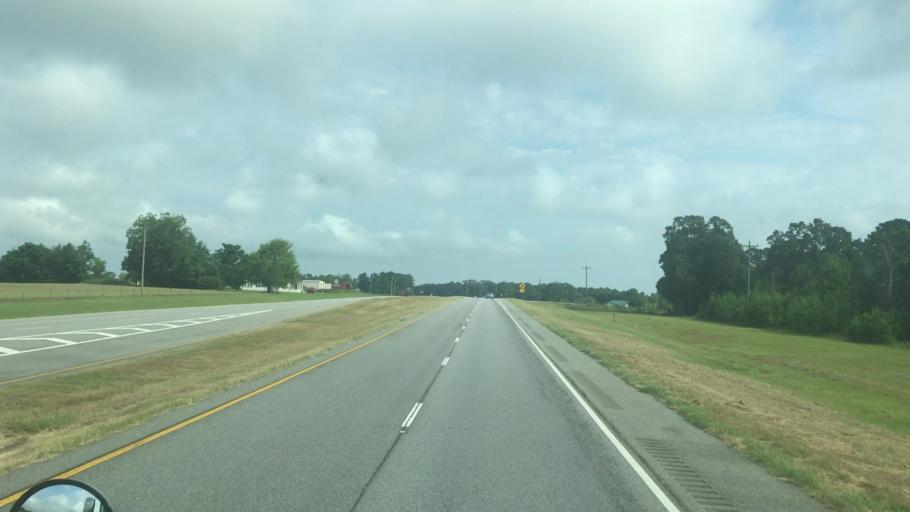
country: US
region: Georgia
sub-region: Miller County
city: Colquitt
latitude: 31.2361
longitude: -84.7857
